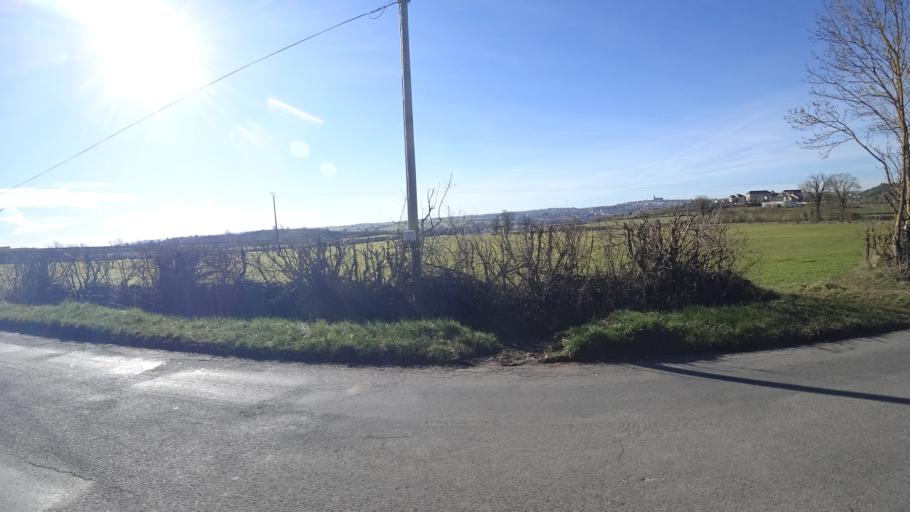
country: FR
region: Midi-Pyrenees
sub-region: Departement de l'Aveyron
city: Sebazac-Concoures
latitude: 44.3881
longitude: 2.5917
